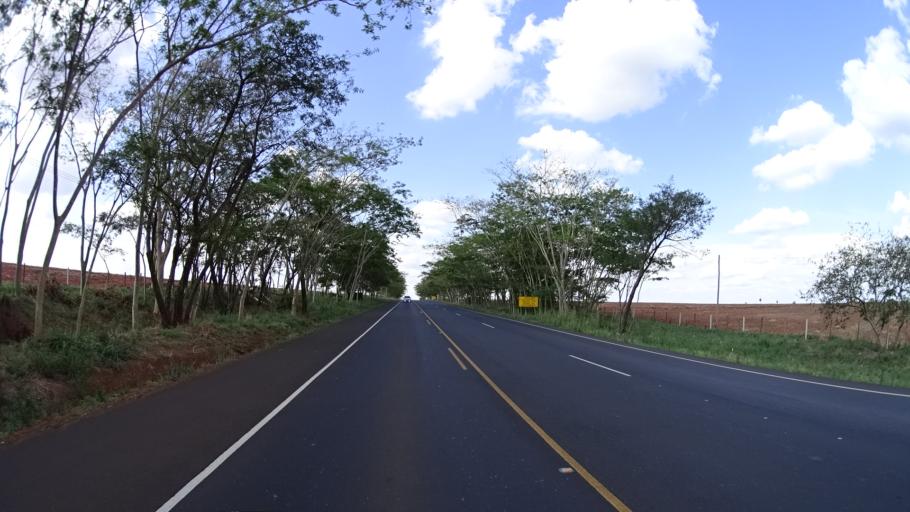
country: BR
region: Sao Paulo
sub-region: Urupes
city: Urupes
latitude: -21.0392
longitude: -49.2424
